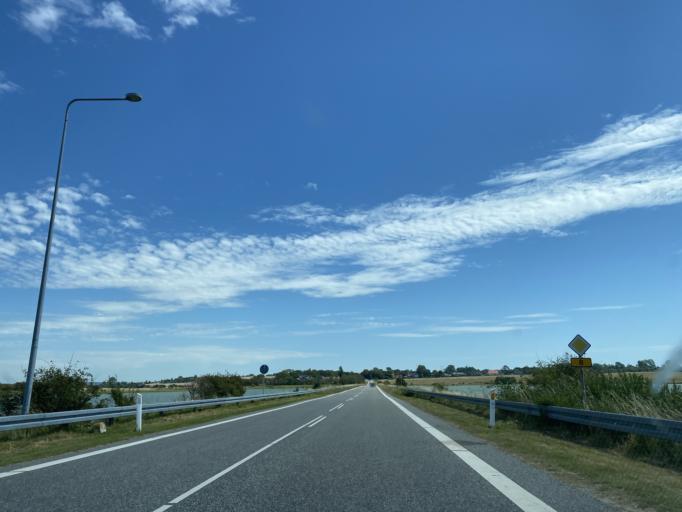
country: DK
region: South Denmark
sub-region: Assens Kommune
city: Harby
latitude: 55.1043
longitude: 10.0856
